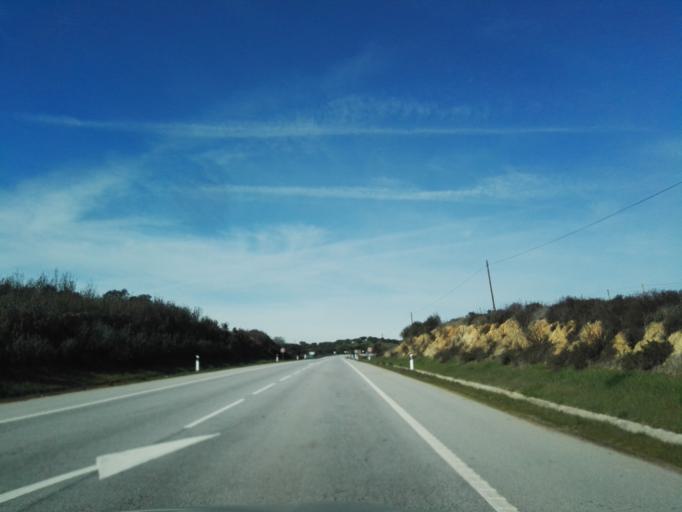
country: PT
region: Portalegre
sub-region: Portalegre
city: Urra
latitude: 39.1946
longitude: -7.3616
